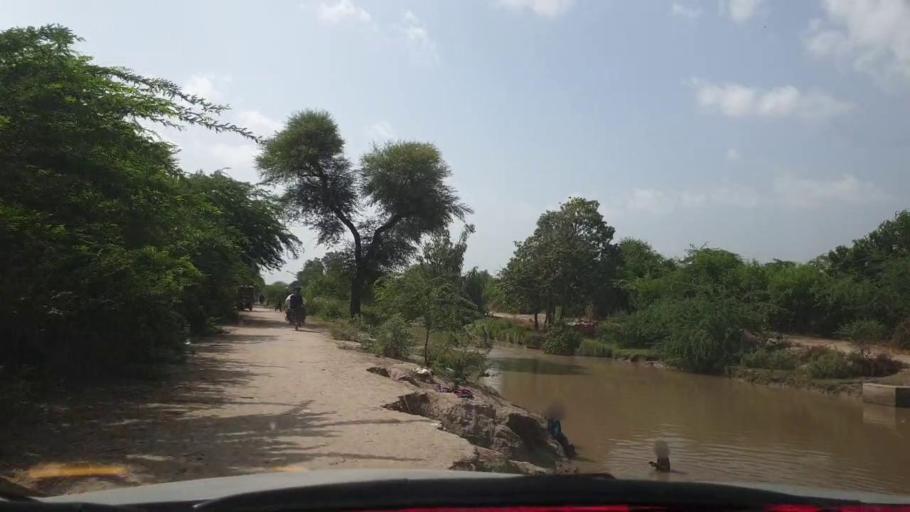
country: PK
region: Sindh
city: Talhar
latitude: 24.8603
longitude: 68.9007
